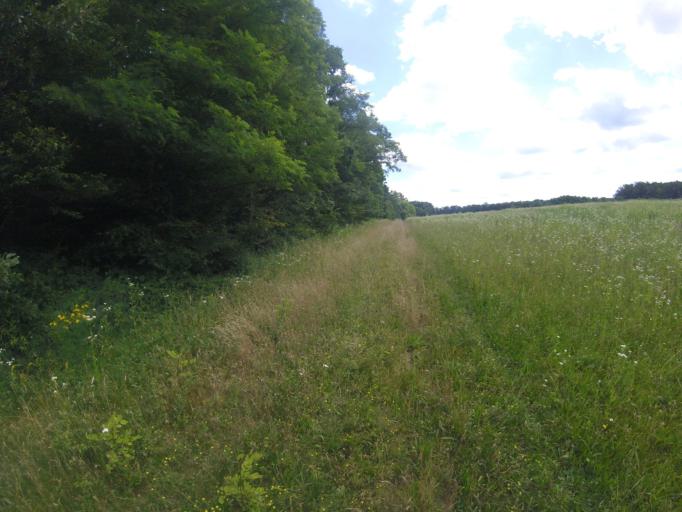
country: HU
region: Zala
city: Zalalovo
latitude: 46.8269
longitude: 16.5529
